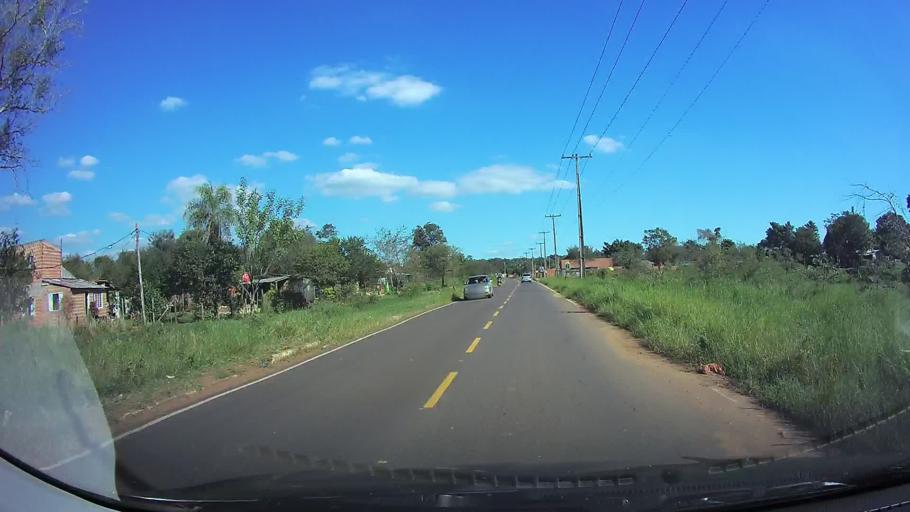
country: PY
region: Central
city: Limpio
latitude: -25.1904
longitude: -57.4751
